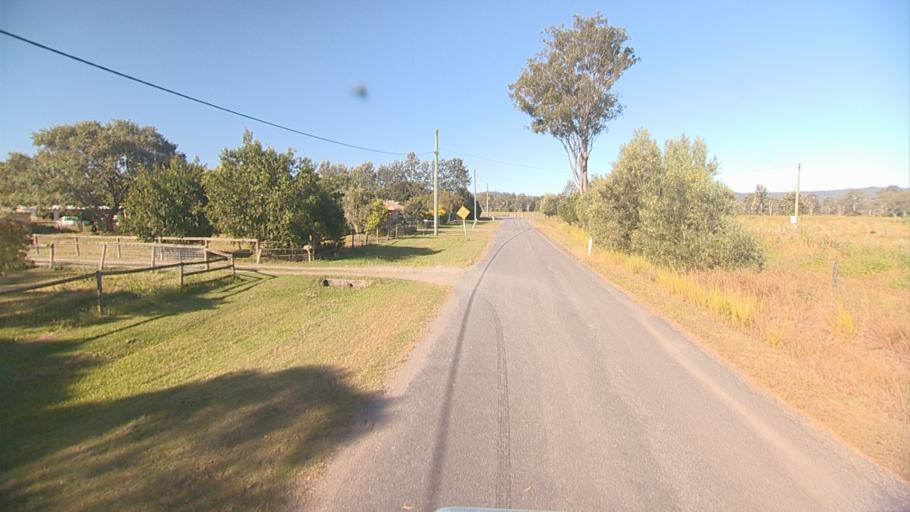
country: AU
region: Queensland
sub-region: Logan
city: Logan Reserve
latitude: -27.7423
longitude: 153.1135
